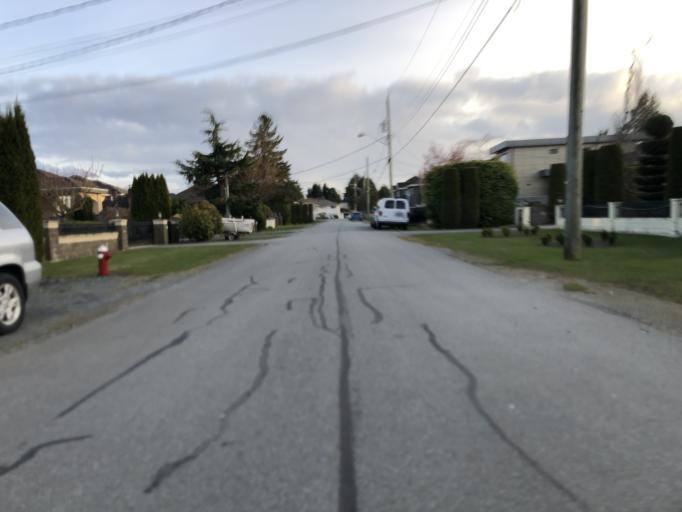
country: CA
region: British Columbia
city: Richmond
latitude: 49.1496
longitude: -123.1270
